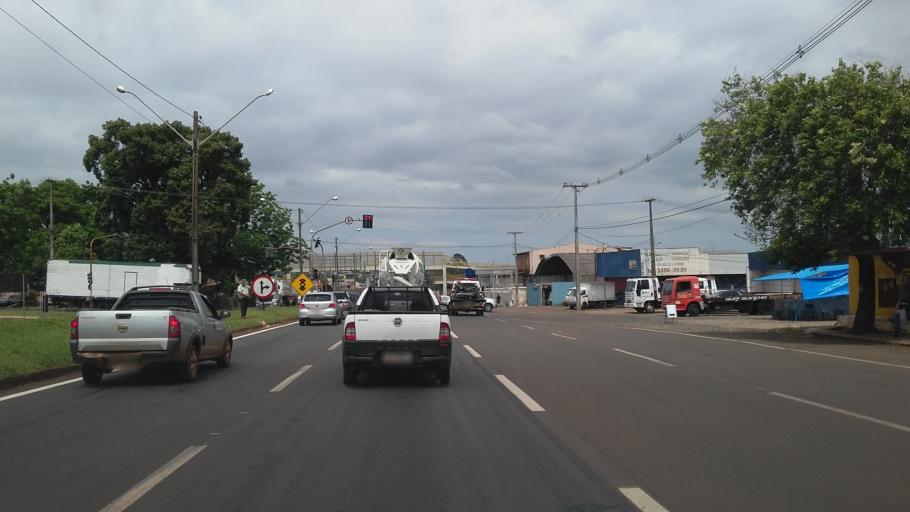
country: BR
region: Parana
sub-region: Londrina
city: Londrina
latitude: -23.2929
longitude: -51.1423
